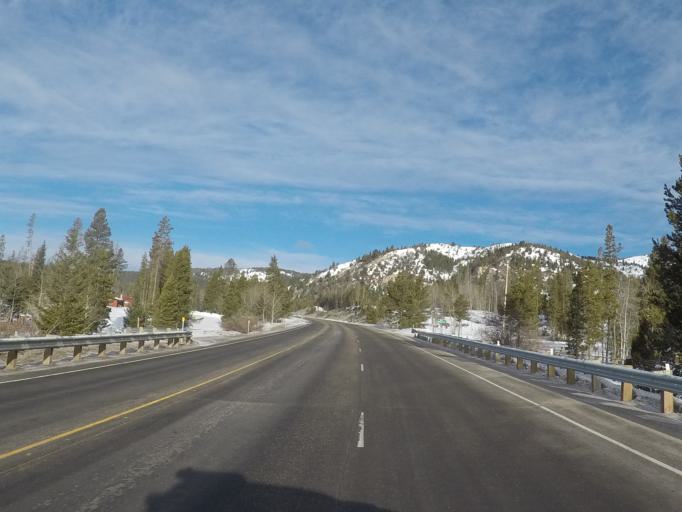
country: US
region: Montana
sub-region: Granite County
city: Philipsburg
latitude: 46.1680
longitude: -113.1576
